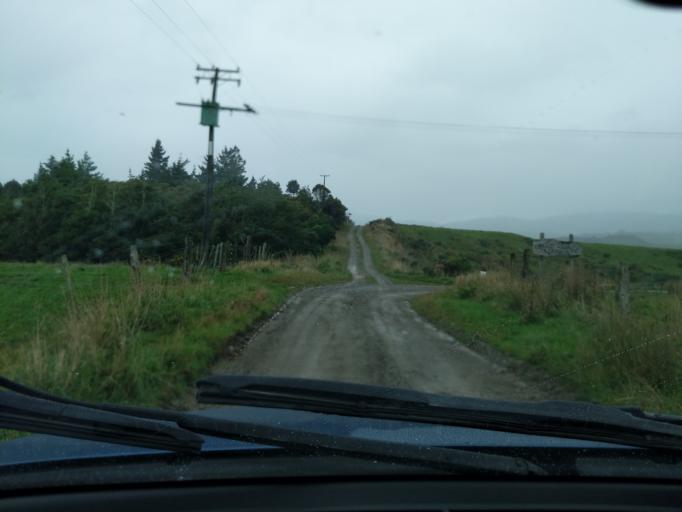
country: NZ
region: Tasman
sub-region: Tasman District
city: Takaka
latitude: -40.6521
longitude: 172.4704
